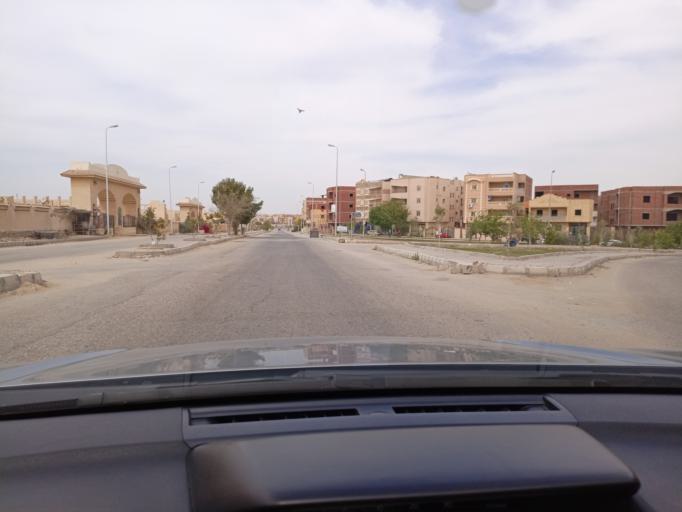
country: EG
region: Muhafazat al Qalyubiyah
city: Al Khankah
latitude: 30.2466
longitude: 31.4955
